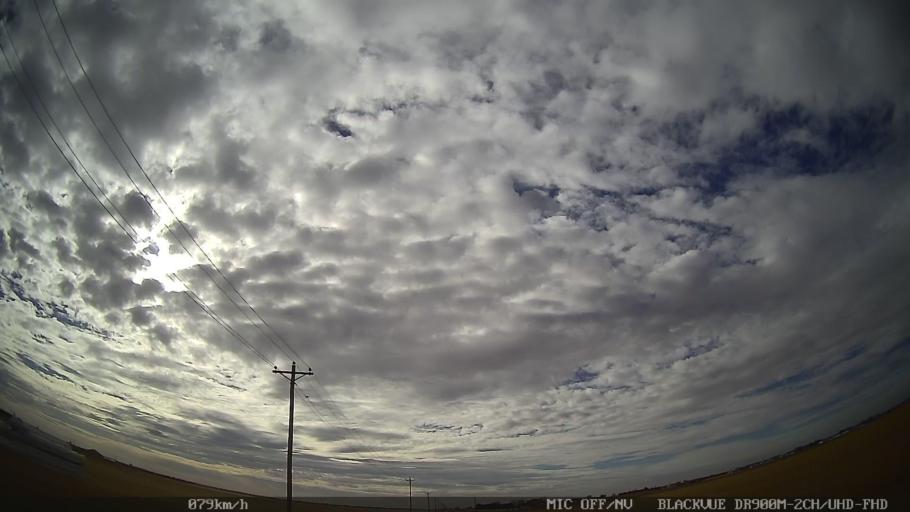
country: US
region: New Mexico
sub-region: Curry County
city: Texico
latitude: 34.4267
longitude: -103.0907
